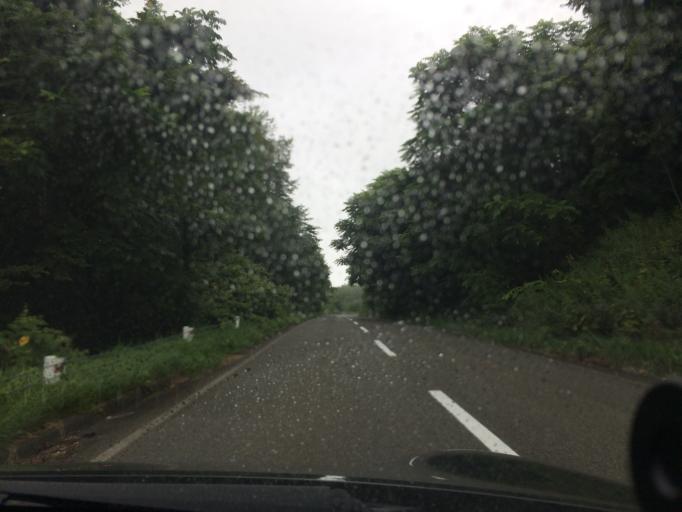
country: JP
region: Hokkaido
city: Otofuke
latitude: 43.0105
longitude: 143.0773
